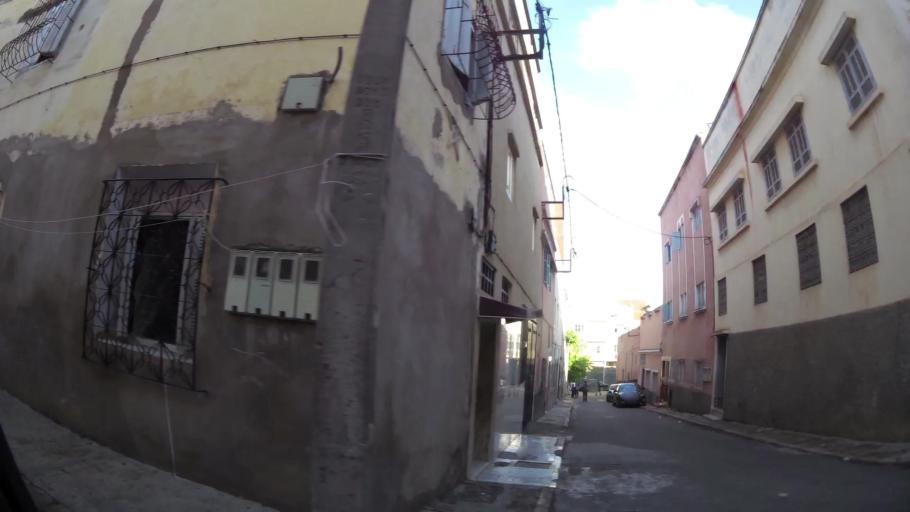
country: MA
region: Chaouia-Ouardigha
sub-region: Settat Province
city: Settat
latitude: 33.0066
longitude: -7.6235
